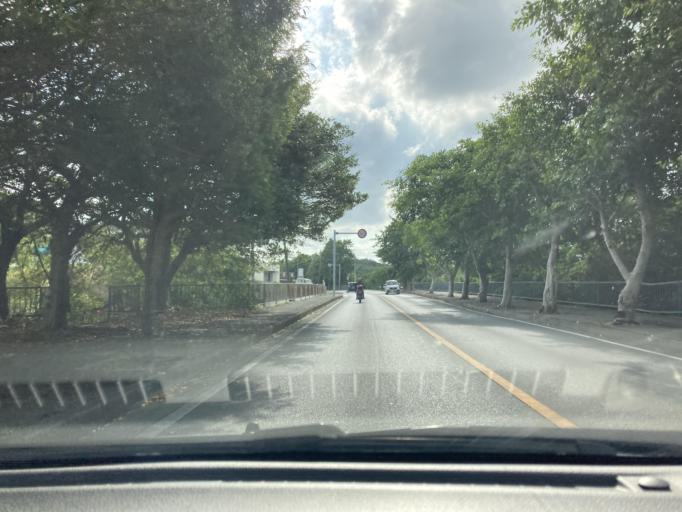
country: JP
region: Okinawa
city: Tomigusuku
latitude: 26.1647
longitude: 127.7343
